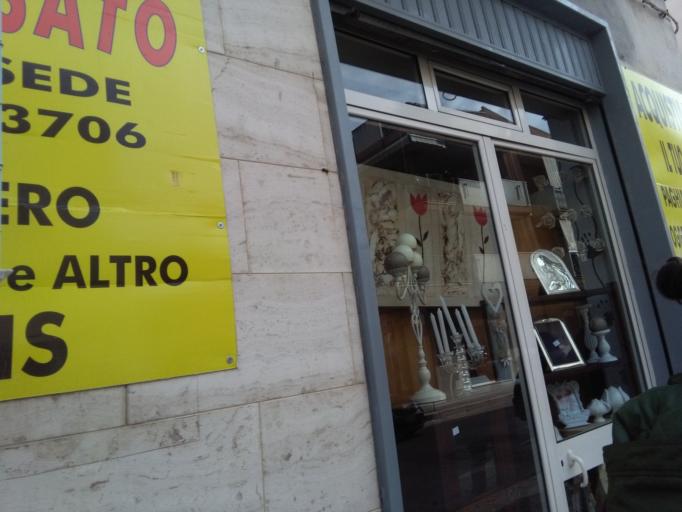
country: IT
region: Apulia
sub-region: Provincia di Barletta - Andria - Trani
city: Andria
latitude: 41.2338
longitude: 16.2948
